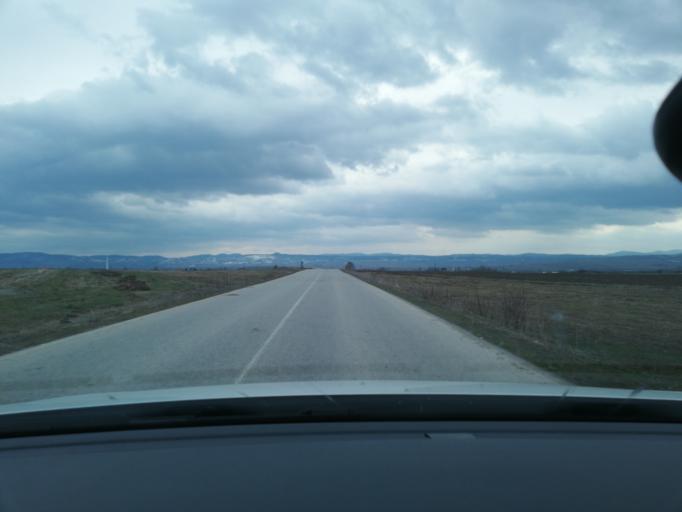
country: TR
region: Bolu
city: Gerede
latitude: 40.7605
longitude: 32.1967
